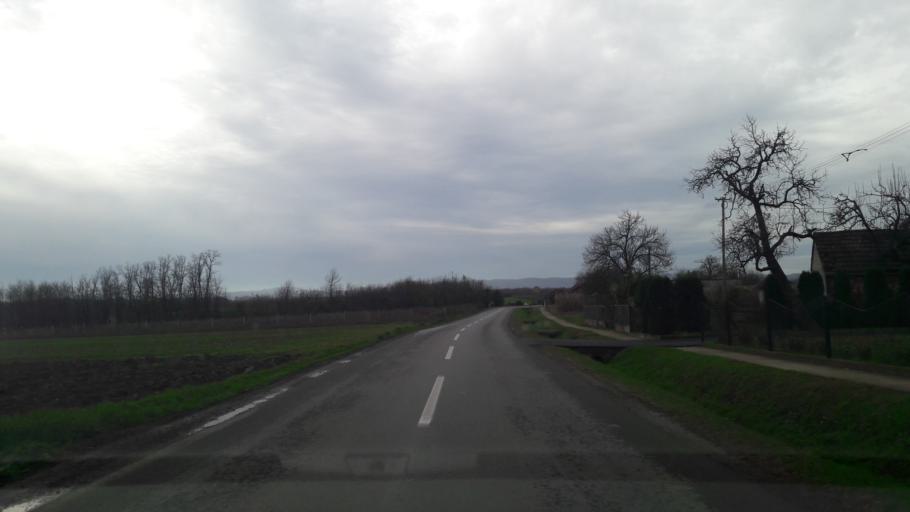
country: HR
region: Osjecko-Baranjska
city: Fericanci
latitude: 45.5253
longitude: 18.0142
